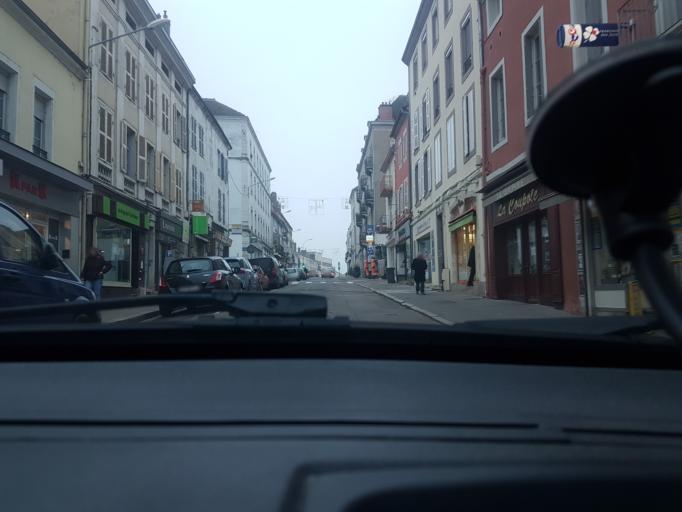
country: FR
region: Bourgogne
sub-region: Departement de Saone-et-Loire
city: Chalon-sur-Saone
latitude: 46.7857
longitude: 4.8521
